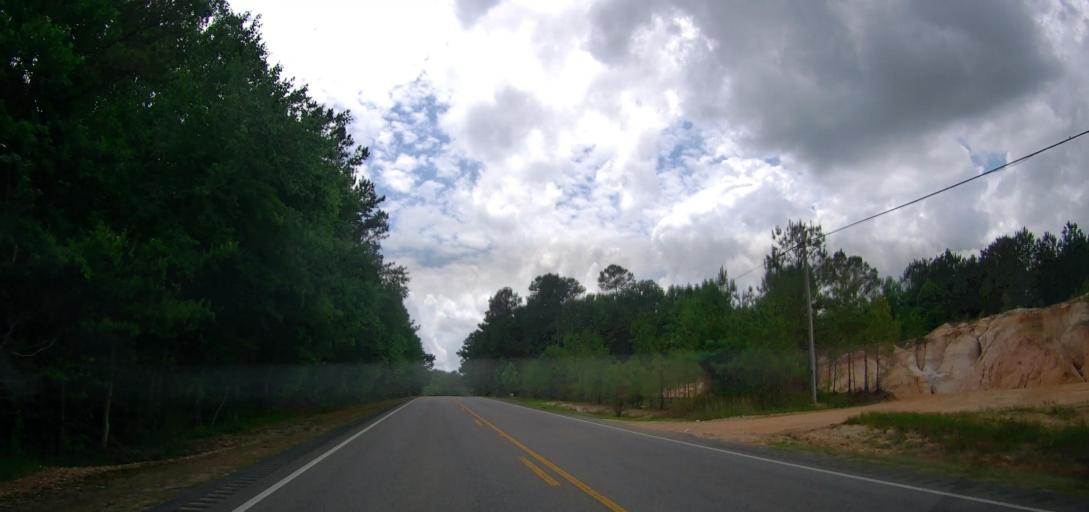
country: US
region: Alabama
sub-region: Marion County
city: Hamilton
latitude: 34.1265
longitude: -88.0328
